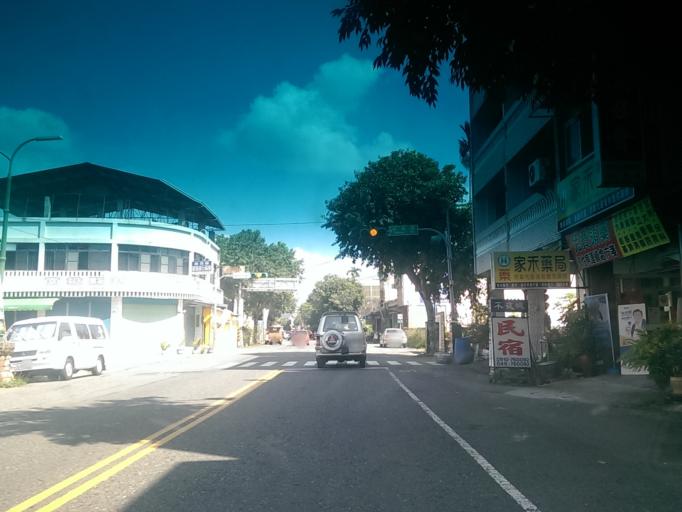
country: TW
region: Taiwan
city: Lugu
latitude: 23.8268
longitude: 120.7787
